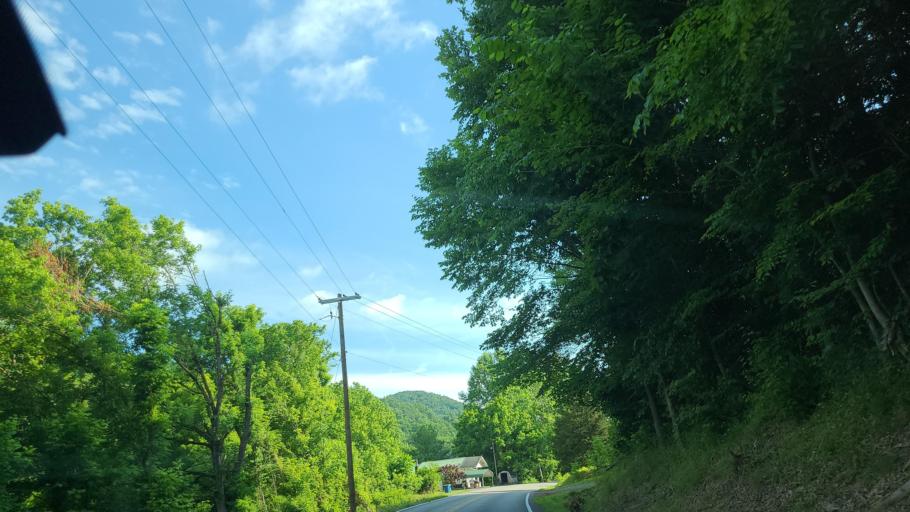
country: US
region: Kentucky
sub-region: Bell County
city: Pineville
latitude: 36.7585
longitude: -83.7819
